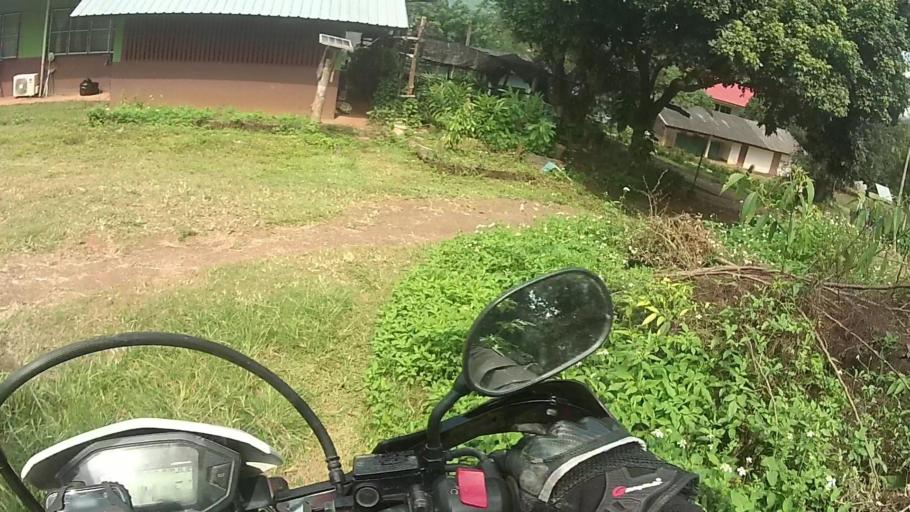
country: TH
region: Chiang Mai
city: Mae Taeng
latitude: 19.0946
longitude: 98.8396
